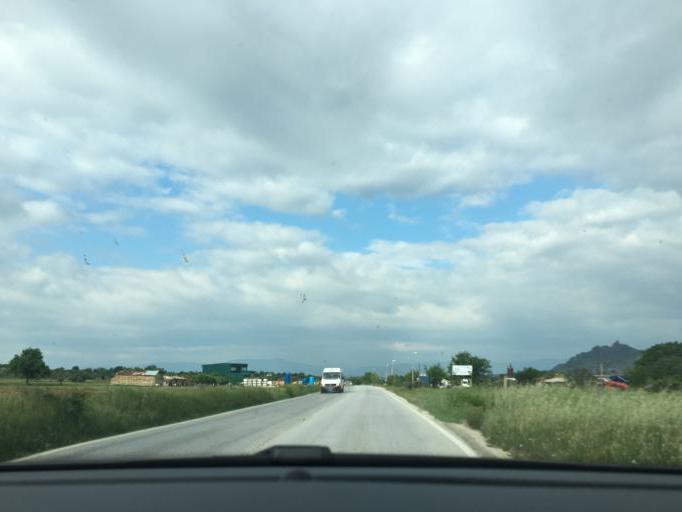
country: MK
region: Prilep
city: Prilep
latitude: 41.3613
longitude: 21.5963
